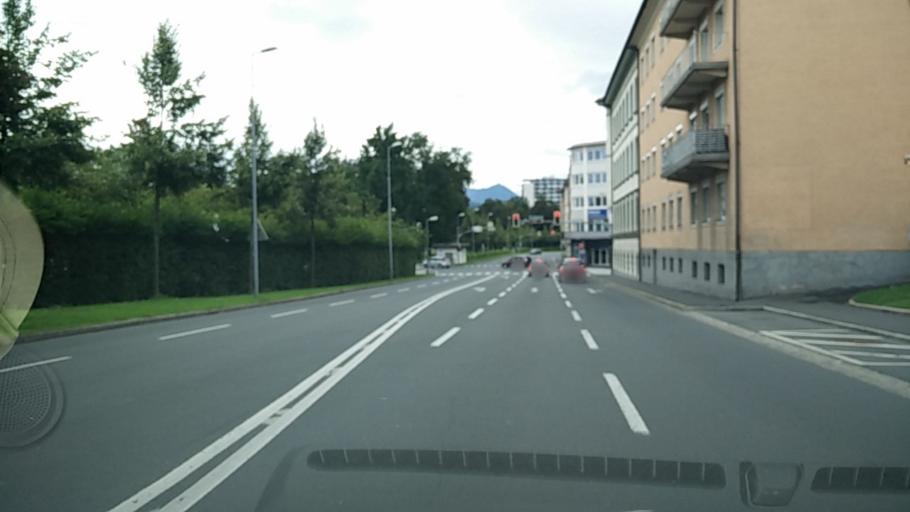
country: AT
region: Carinthia
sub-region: Klagenfurt am Woerthersee
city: Klagenfurt am Woerthersee
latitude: 46.6278
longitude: 14.3018
